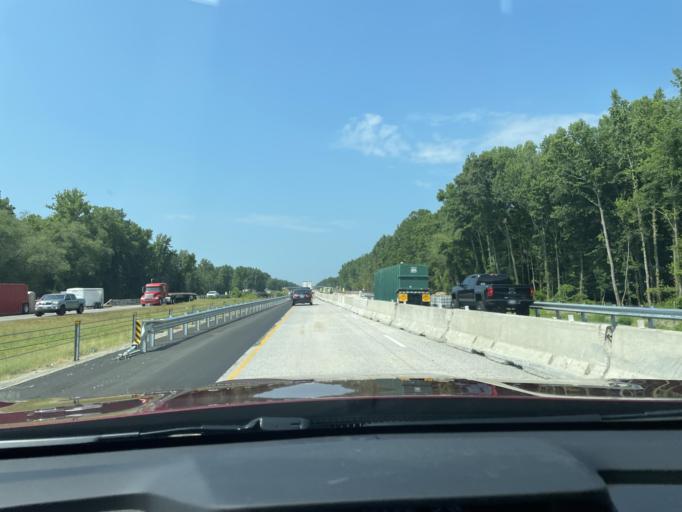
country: US
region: Arkansas
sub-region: White County
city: Searcy
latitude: 35.1785
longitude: -91.7613
